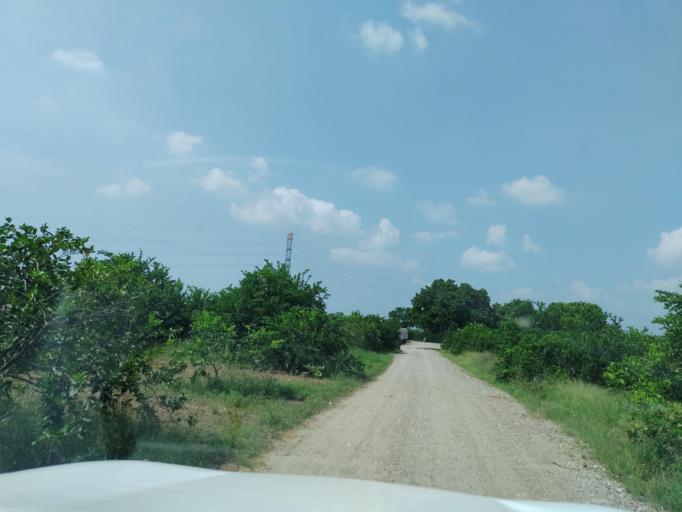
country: MX
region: Veracruz
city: Martinez de la Torre
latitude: 20.0895
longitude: -97.0526
